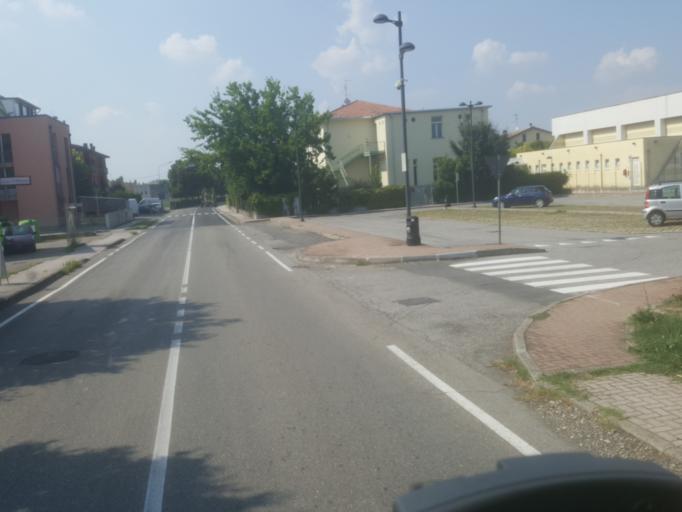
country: IT
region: Emilia-Romagna
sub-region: Provincia di Parma
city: Torrile
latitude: 44.9220
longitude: 10.3268
